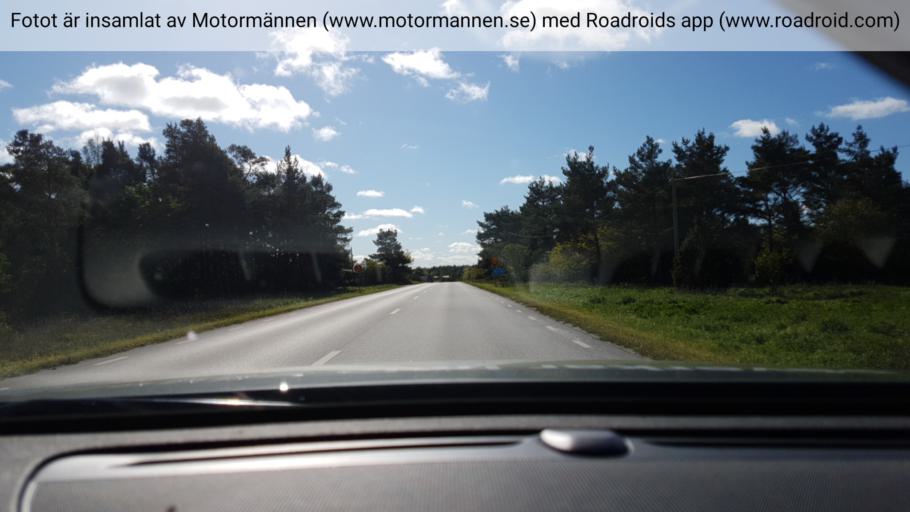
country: SE
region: Gotland
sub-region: Gotland
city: Slite
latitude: 57.7274
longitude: 18.7893
